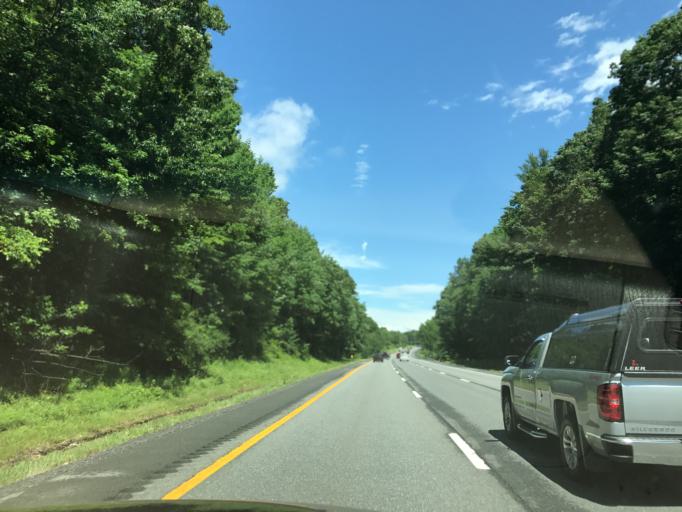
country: US
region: New York
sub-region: Warren County
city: West Glens Falls
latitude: 43.1822
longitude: -73.7073
